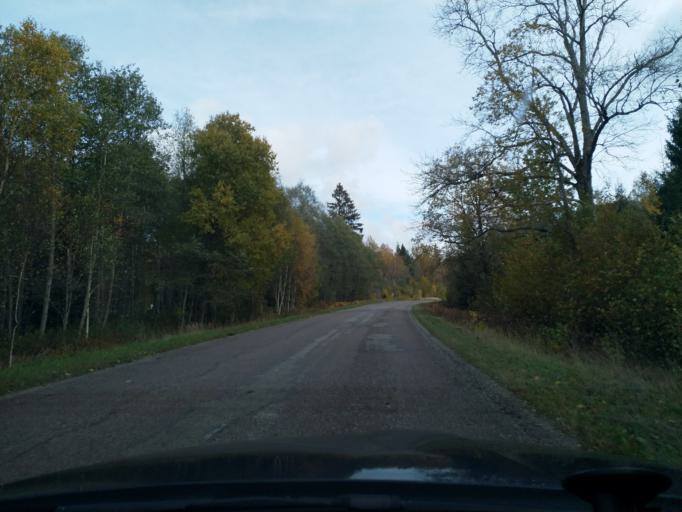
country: LV
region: Dundaga
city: Dundaga
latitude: 57.5509
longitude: 22.3573
